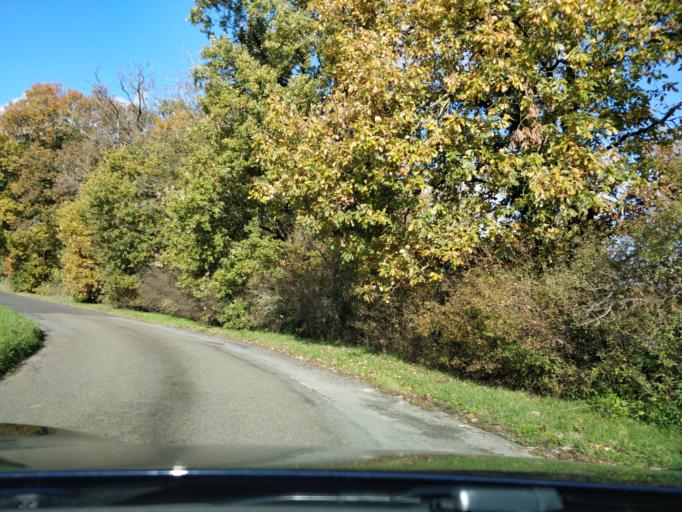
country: FR
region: Ile-de-France
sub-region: Departement de l'Essonne
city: Fontenay-les-Briis
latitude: 48.6283
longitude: 2.1631
